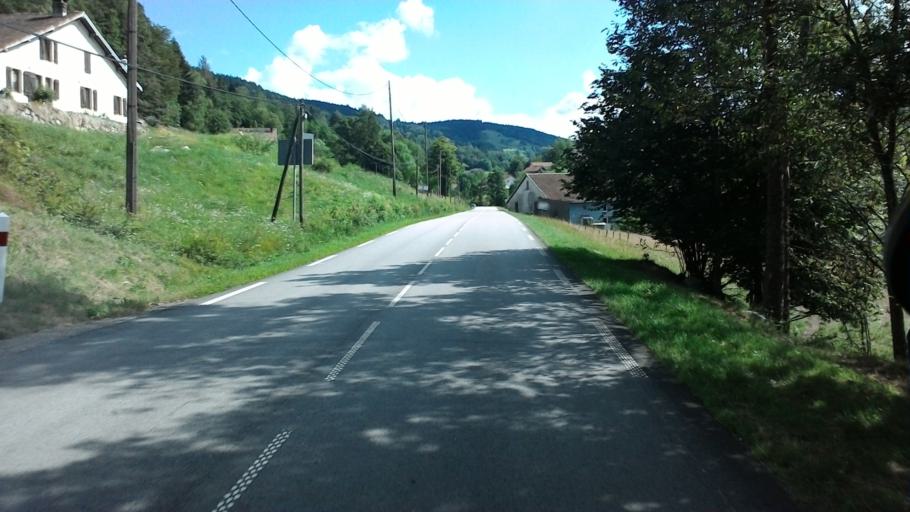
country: FR
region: Lorraine
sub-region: Departement des Vosges
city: Le Menil
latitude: 47.9125
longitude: 6.7873
